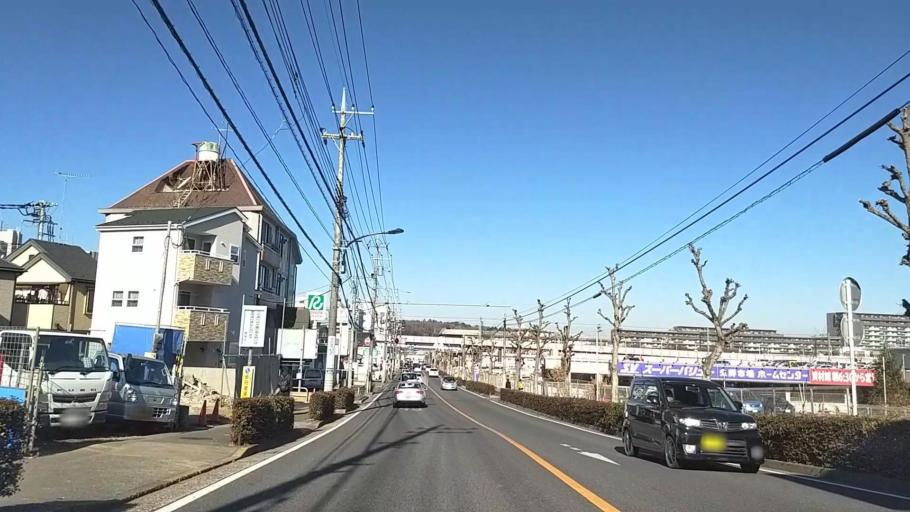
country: JP
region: Tokyo
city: Hachioji
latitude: 35.6396
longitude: 139.2871
